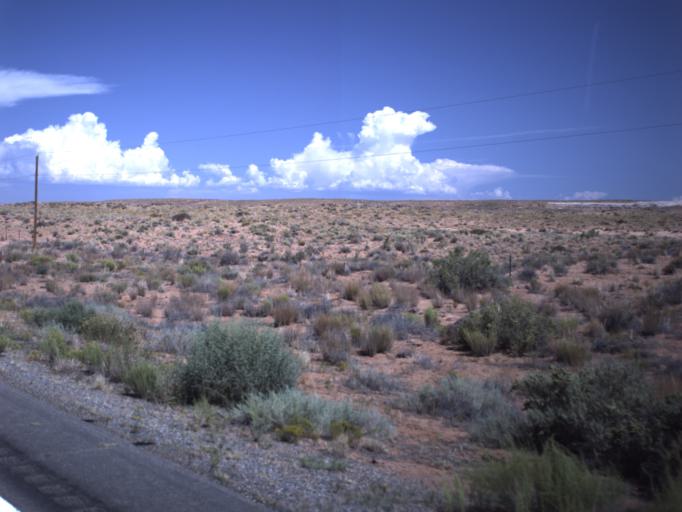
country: US
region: Utah
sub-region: San Juan County
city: Blanding
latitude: 37.1364
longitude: -109.5552
